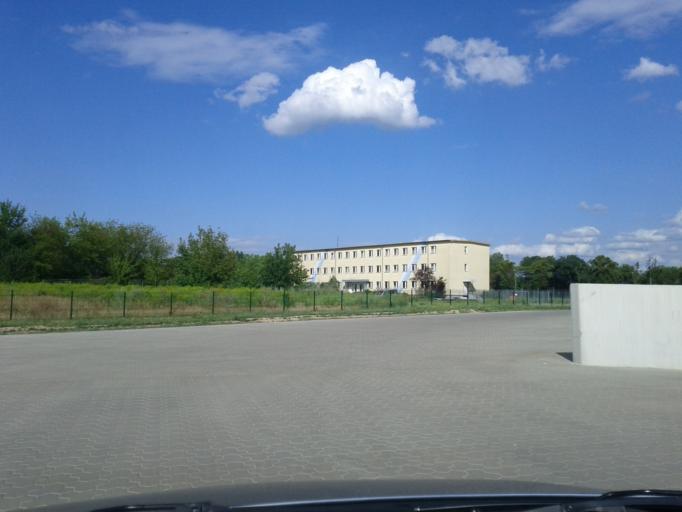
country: DE
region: Brandenburg
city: Hoppegarten
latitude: 52.5114
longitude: 13.6485
